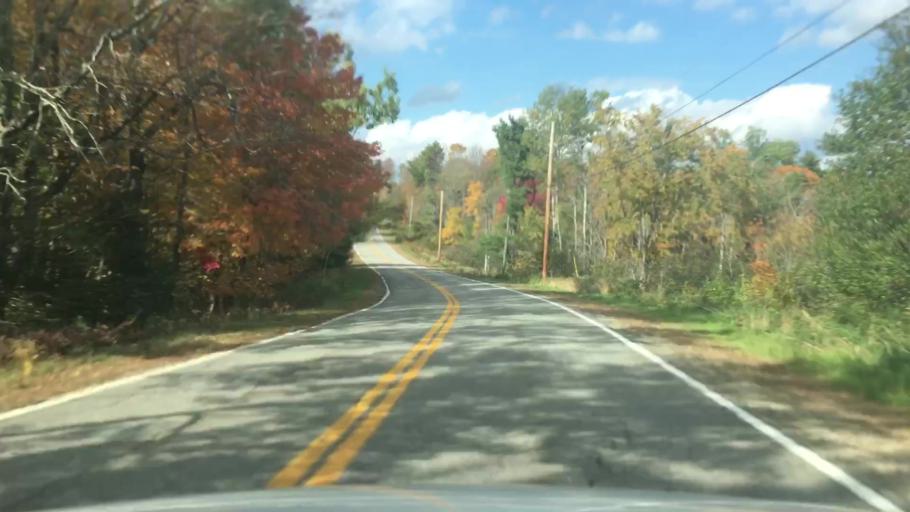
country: US
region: Maine
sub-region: Knox County
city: Washington
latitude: 44.3161
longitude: -69.3549
